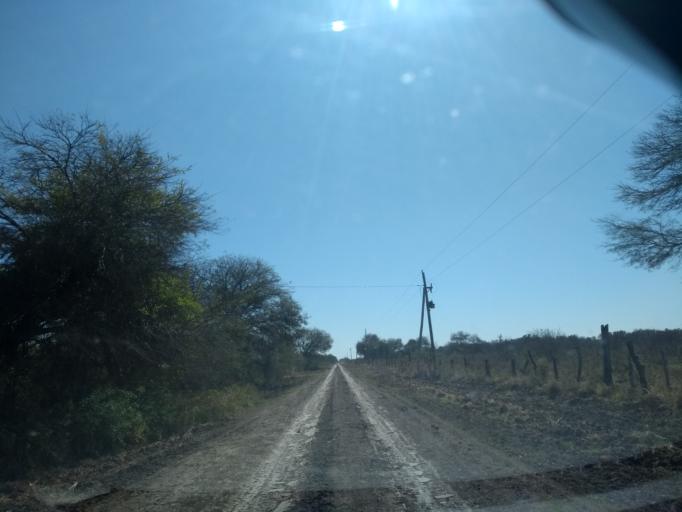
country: AR
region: Chaco
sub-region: Departamento de Quitilipi
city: Quitilipi
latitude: -26.7453
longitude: -60.2381
